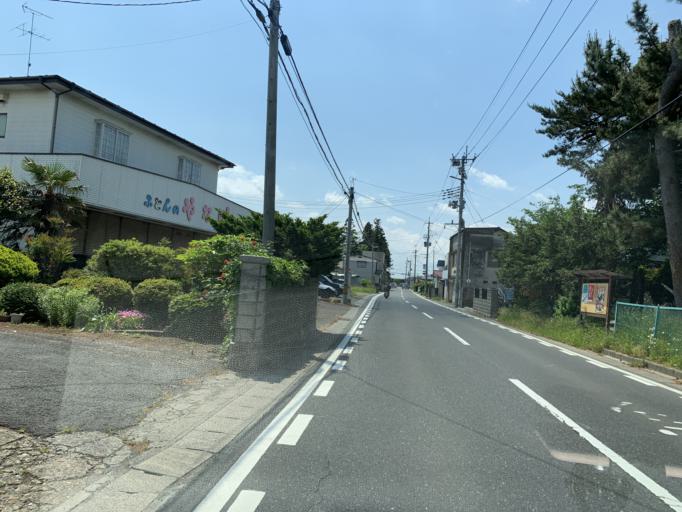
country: JP
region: Miyagi
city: Kogota
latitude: 38.5787
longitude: 141.0329
